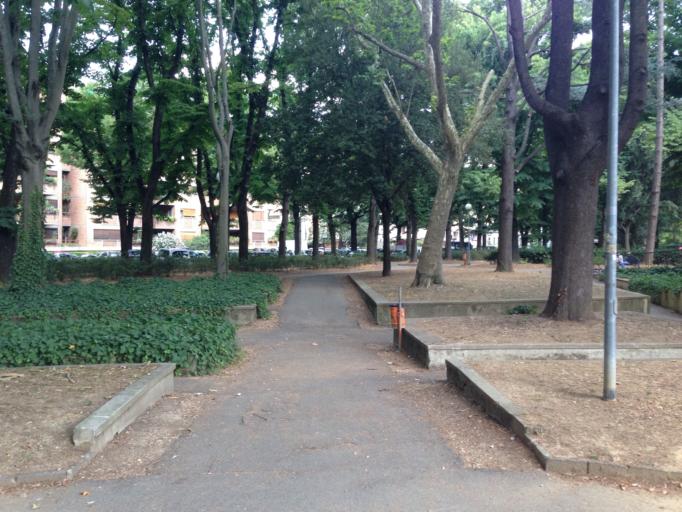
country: IT
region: Tuscany
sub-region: Province of Florence
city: Florence
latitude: 43.7655
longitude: 11.2728
